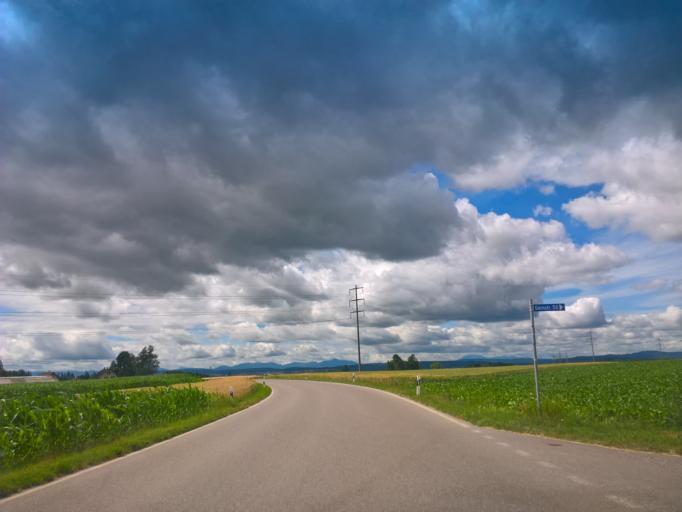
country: CH
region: Zurich
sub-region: Bezirk Winterthur
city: Brutten
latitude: 47.4668
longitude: 8.6674
